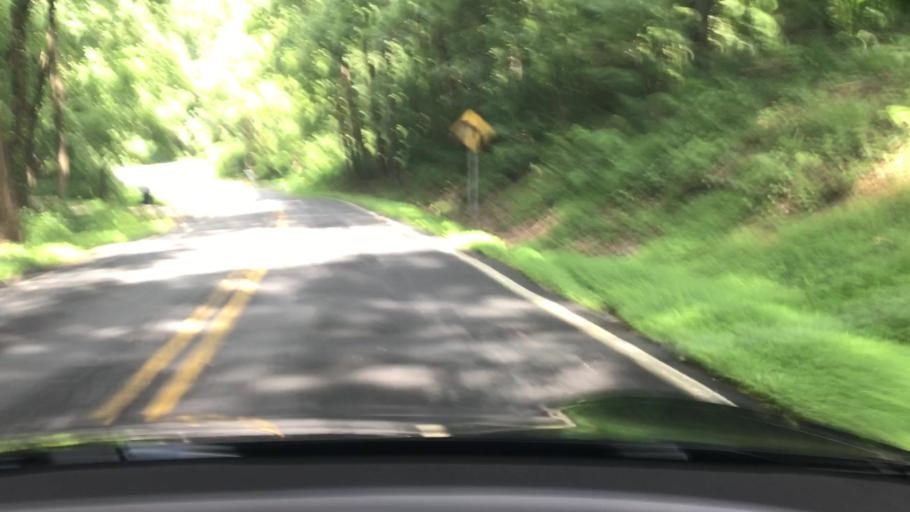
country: US
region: Pennsylvania
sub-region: Cumberland County
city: New Cumberland
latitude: 40.1886
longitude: -76.8721
